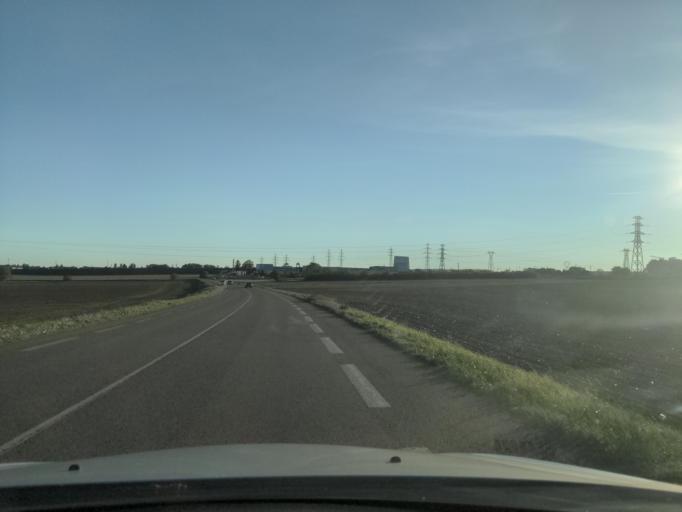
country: FR
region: Bourgogne
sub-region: Departement de la Cote-d'Or
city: Ruffey-les-Echirey
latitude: 47.3624
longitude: 5.0691
